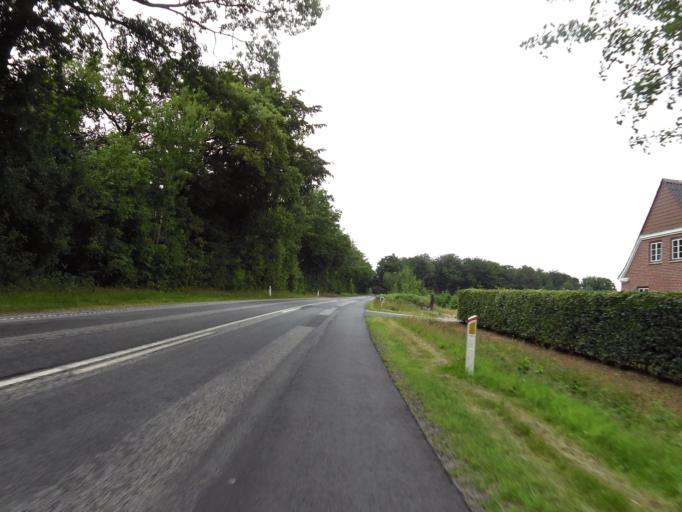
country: DK
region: South Denmark
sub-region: Tonder Kommune
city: Toftlund
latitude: 55.1891
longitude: 8.9606
